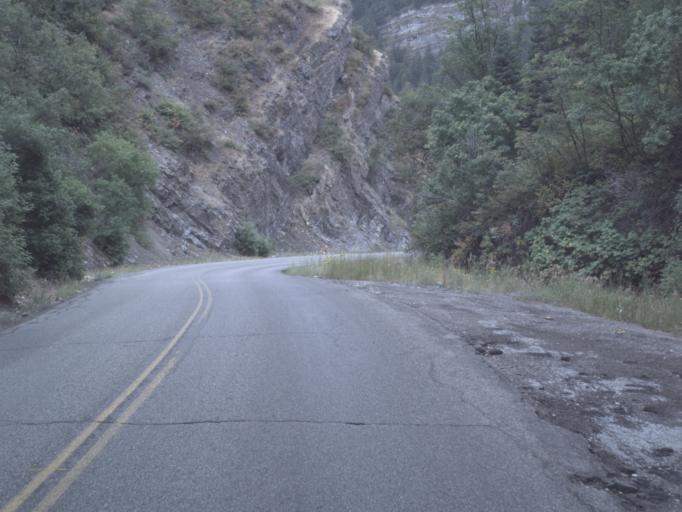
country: US
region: Utah
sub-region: Utah County
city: Orem
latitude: 40.3766
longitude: -111.5680
